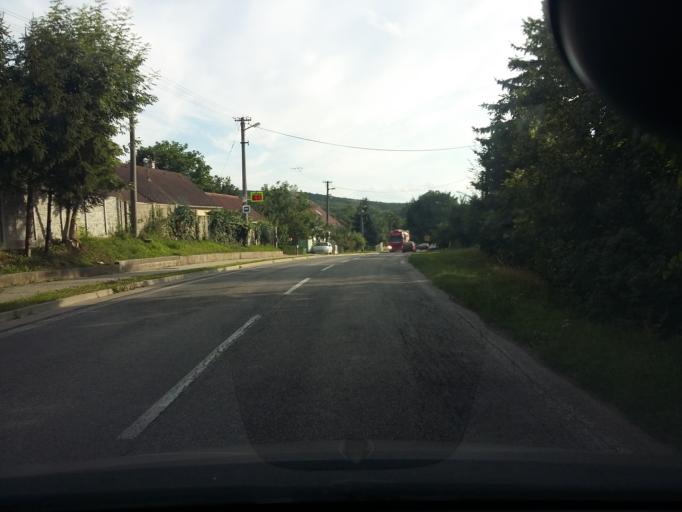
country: SK
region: Bratislavsky
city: Svaty Jur
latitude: 48.3704
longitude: 17.1466
